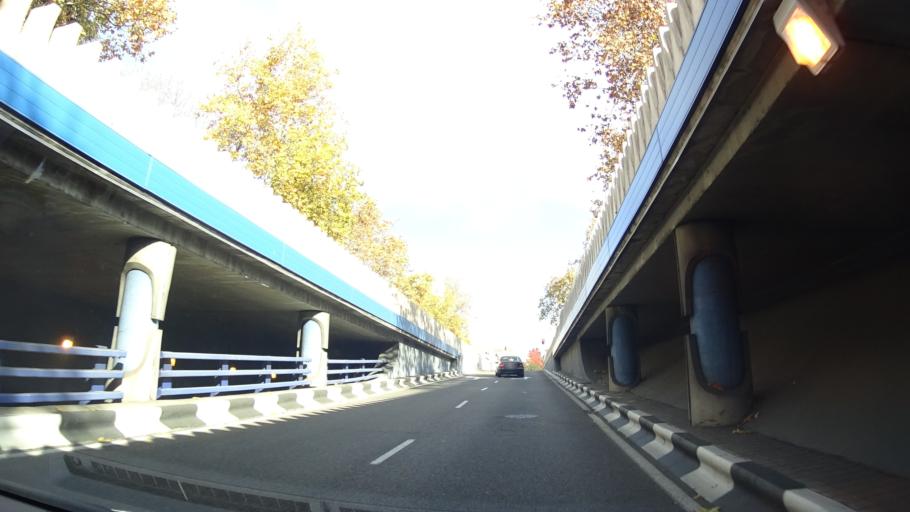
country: ES
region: Madrid
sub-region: Provincia de Madrid
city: Salamanca
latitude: 40.4384
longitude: -3.6842
